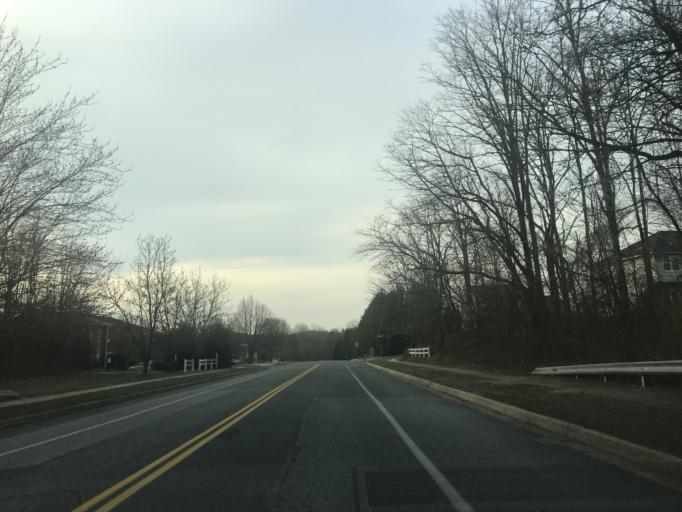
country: US
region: Maryland
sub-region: Harford County
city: South Bel Air
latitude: 39.5404
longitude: -76.3184
